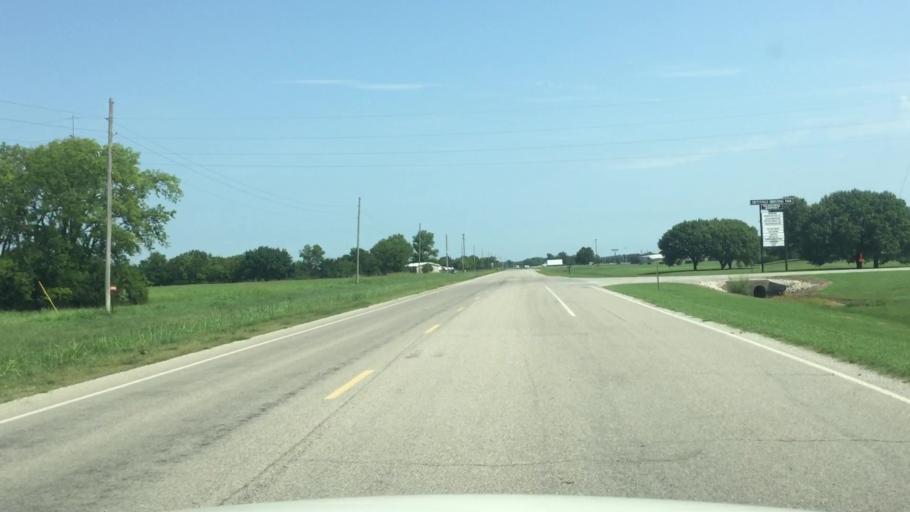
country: US
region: Kansas
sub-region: Montgomery County
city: Coffeyville
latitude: 37.0943
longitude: -95.5861
